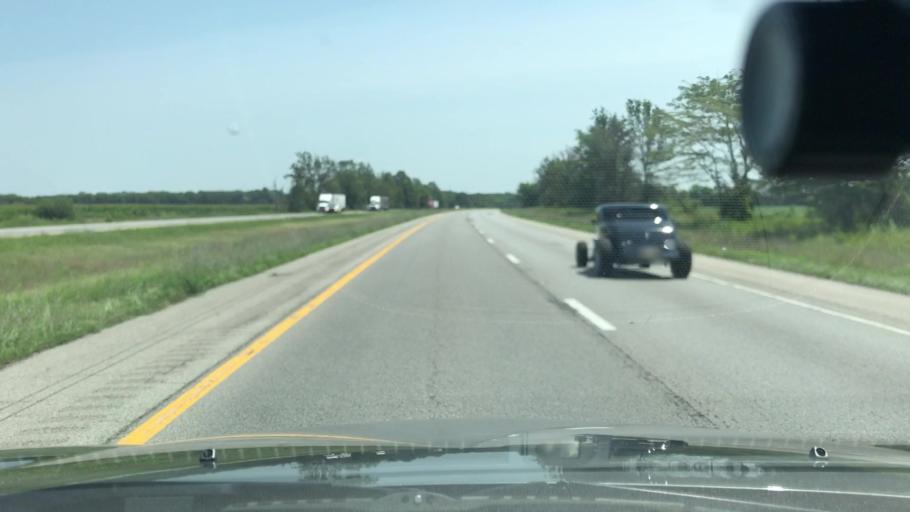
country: US
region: Illinois
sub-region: Clinton County
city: Wamac
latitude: 38.3868
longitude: -89.1366
